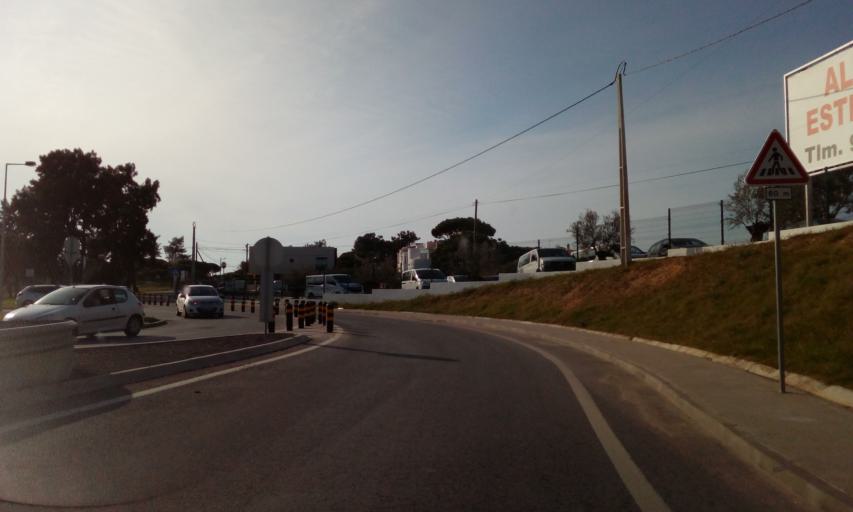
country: PT
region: Faro
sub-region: Faro
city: Faro
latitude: 37.0237
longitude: -7.9706
